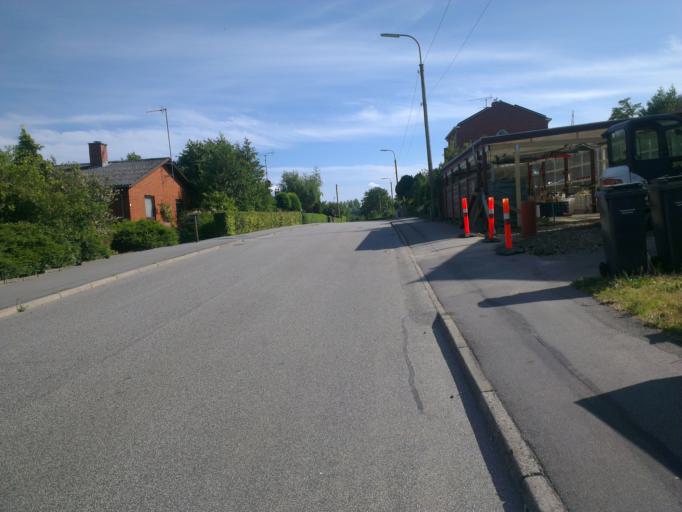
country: DK
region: Capital Region
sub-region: Frederikssund Kommune
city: Skibby
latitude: 55.7498
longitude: 11.9657
